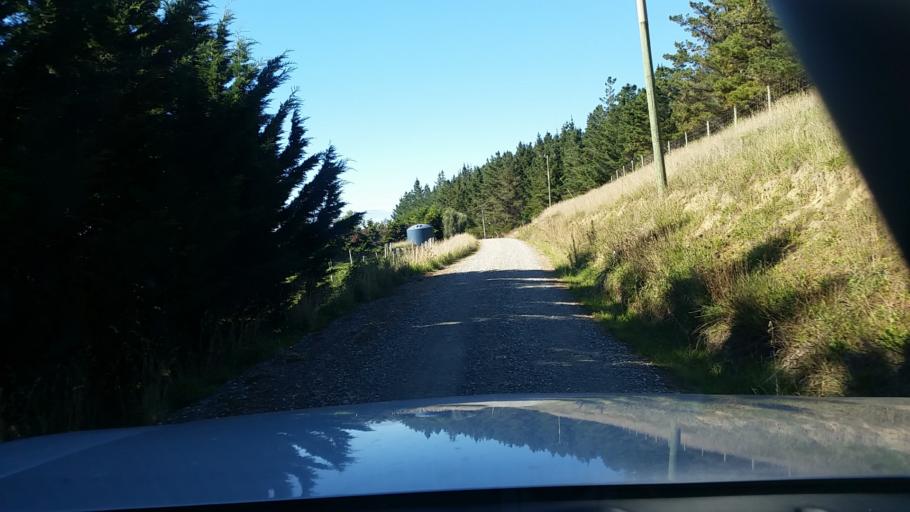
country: NZ
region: Marlborough
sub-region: Marlborough District
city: Blenheim
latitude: -41.6660
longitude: 174.1545
